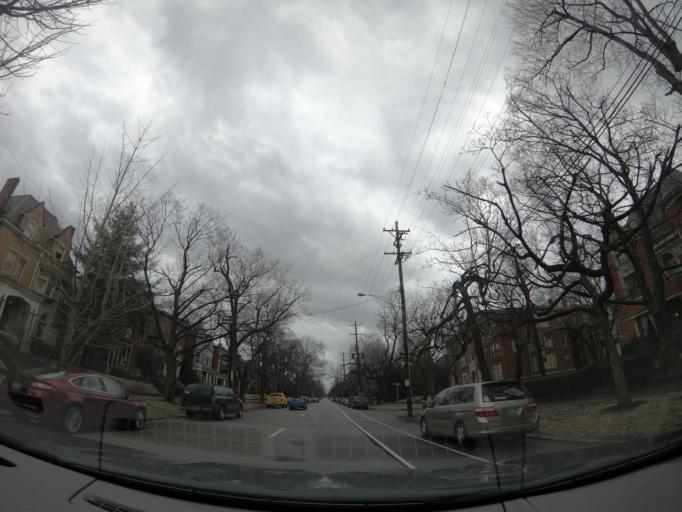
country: US
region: Kentucky
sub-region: Jefferson County
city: Louisville
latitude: 38.2315
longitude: -85.7593
